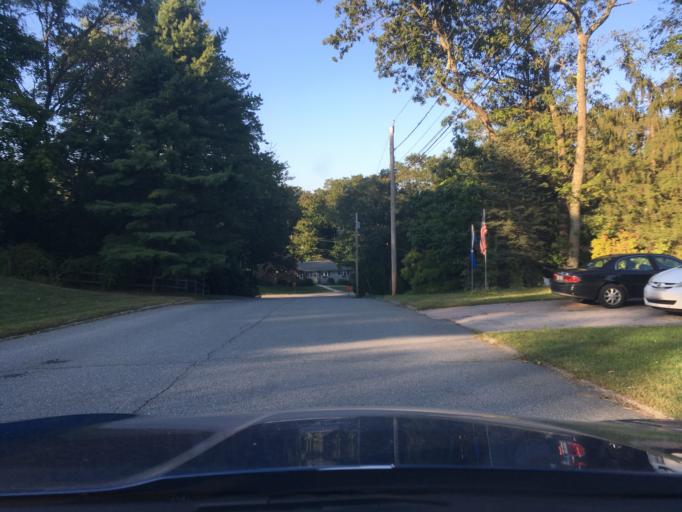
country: US
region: Rhode Island
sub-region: Kent County
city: East Greenwich
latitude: 41.6430
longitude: -71.4719
